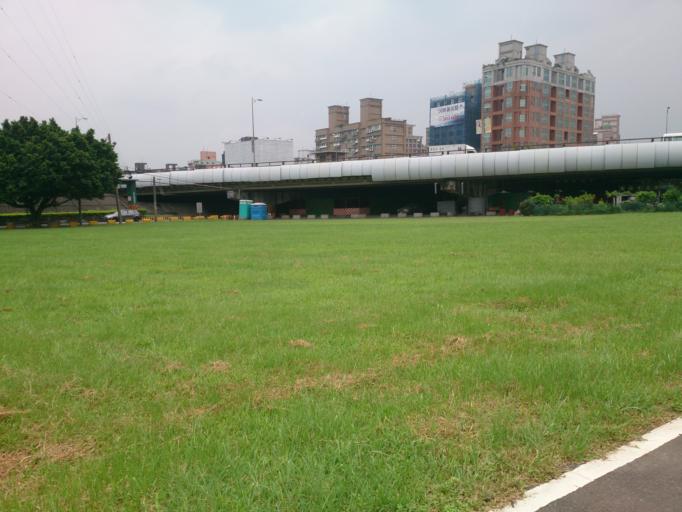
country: TW
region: Taipei
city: Taipei
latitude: 25.0877
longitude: 121.5130
